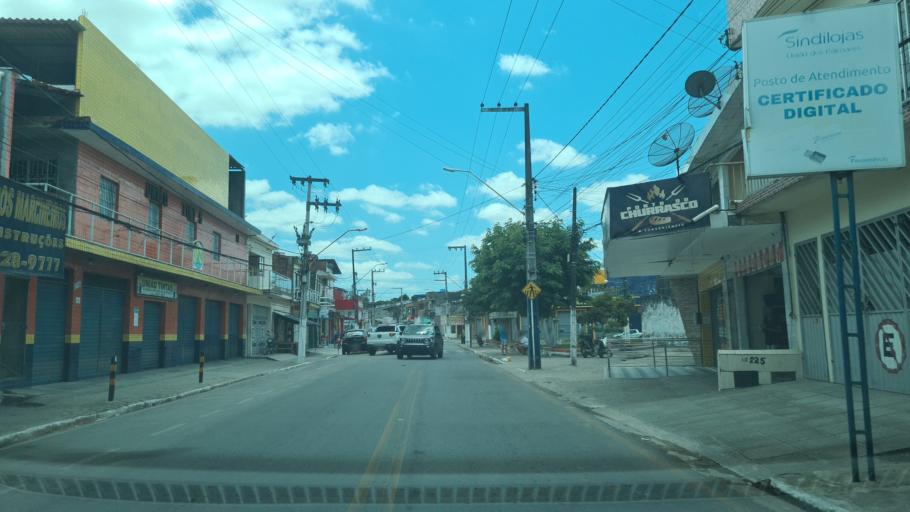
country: BR
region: Alagoas
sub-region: Uniao Dos Palmares
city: Uniao dos Palmares
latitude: -9.1611
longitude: -36.0293
